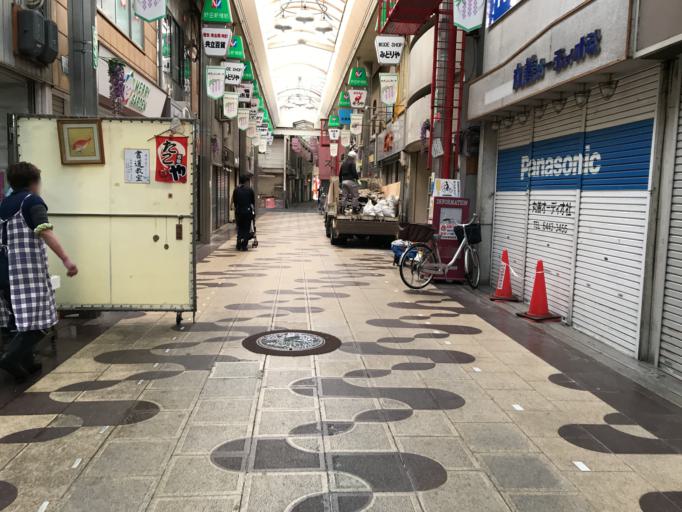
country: JP
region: Osaka
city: Osaka-shi
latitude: 34.6914
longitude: 135.4760
